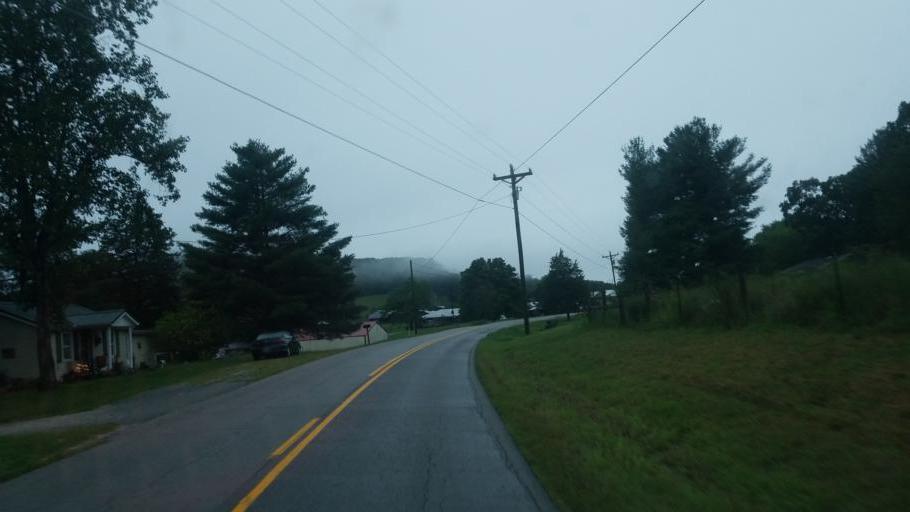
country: US
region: Kentucky
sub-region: Fleming County
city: Flemingsburg
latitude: 38.4046
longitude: -83.6393
